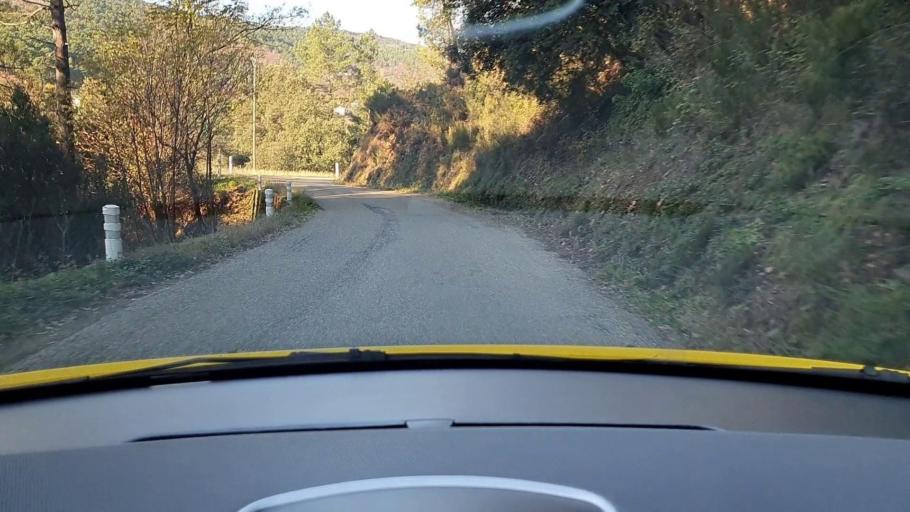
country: FR
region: Languedoc-Roussillon
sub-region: Departement du Gard
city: Branoux-les-Taillades
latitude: 44.2593
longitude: 3.9781
